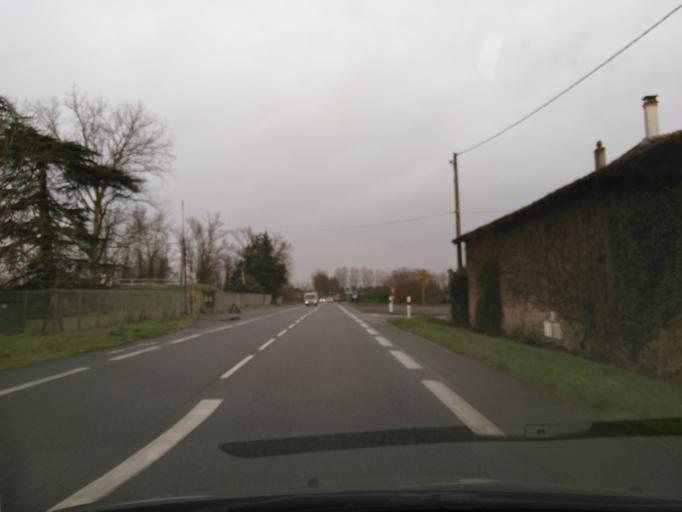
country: FR
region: Midi-Pyrenees
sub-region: Departement de la Haute-Garonne
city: Carbonne
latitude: 43.2876
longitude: 1.2169
